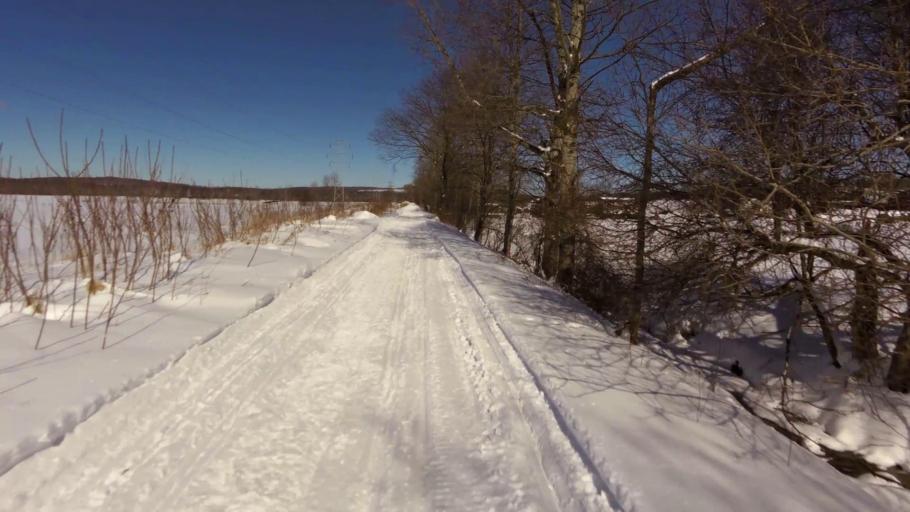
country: US
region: New York
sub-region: Chautauqua County
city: Celoron
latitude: 42.2307
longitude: -79.2685
